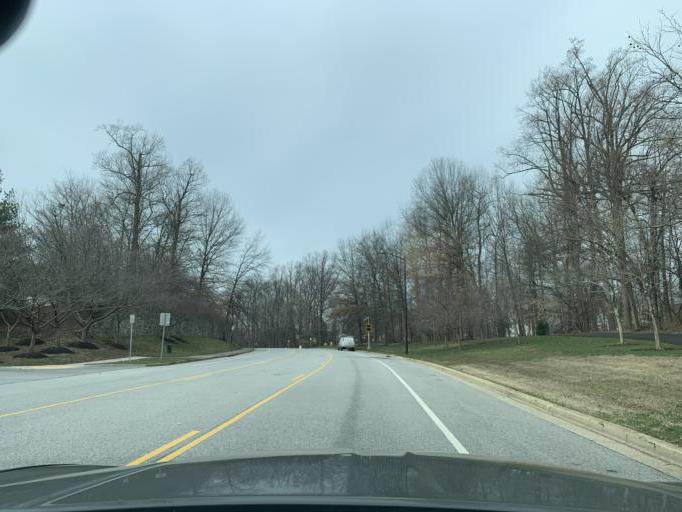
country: US
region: Maryland
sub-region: Howard County
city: Fort George G Mead Junction
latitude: 39.1089
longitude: -76.7997
